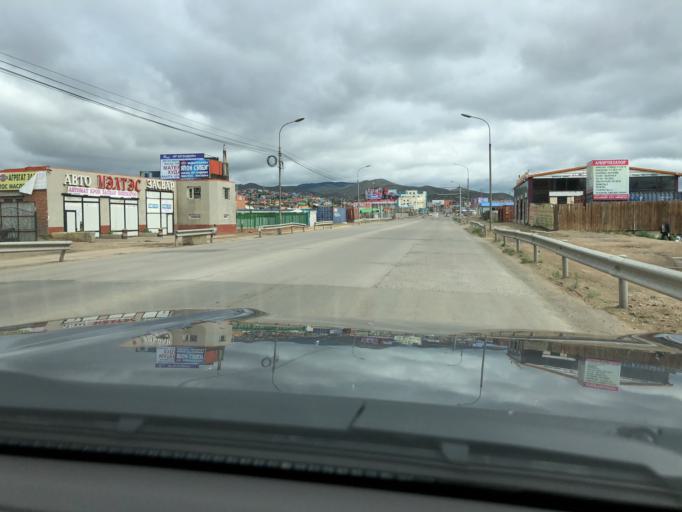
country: MN
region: Ulaanbaatar
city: Ulaanbaatar
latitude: 47.9372
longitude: 106.9157
